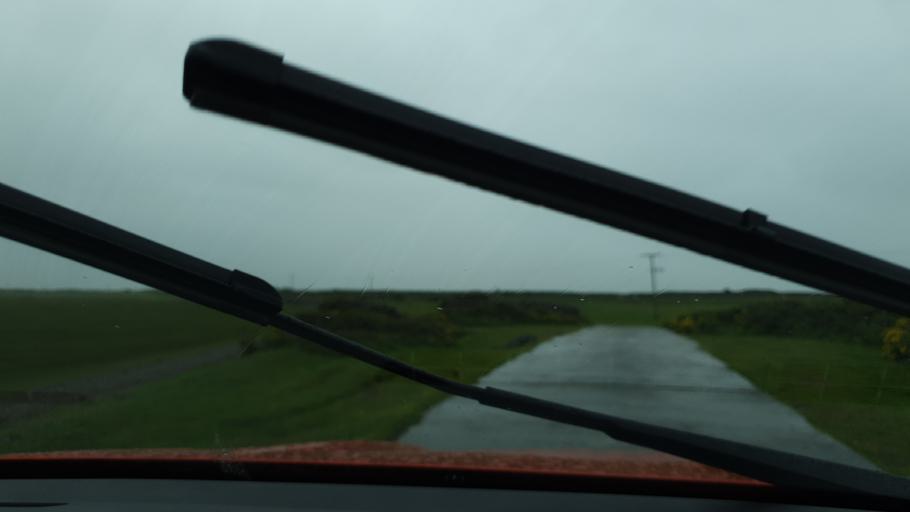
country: GB
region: England
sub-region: Cumbria
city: Barrow in Furness
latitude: 54.0530
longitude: -3.2067
